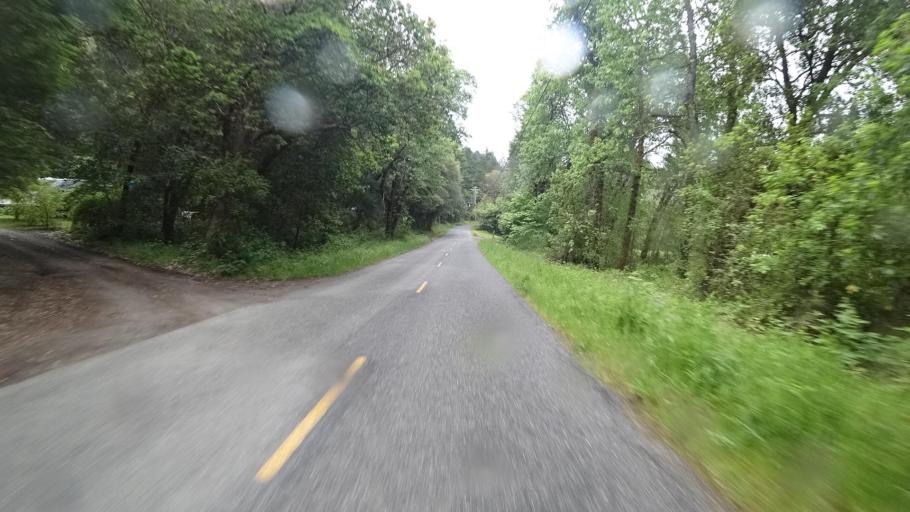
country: US
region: California
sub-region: Humboldt County
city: Willow Creek
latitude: 41.0459
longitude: -123.6616
